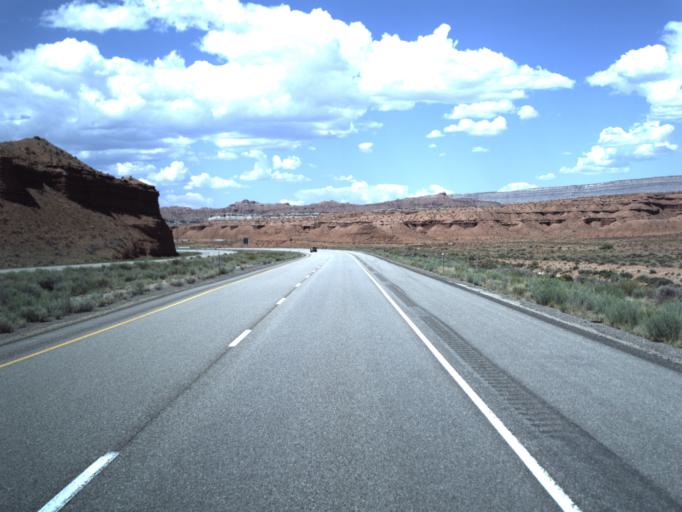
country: US
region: Utah
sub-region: Emery County
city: Ferron
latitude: 38.8455
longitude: -111.0527
